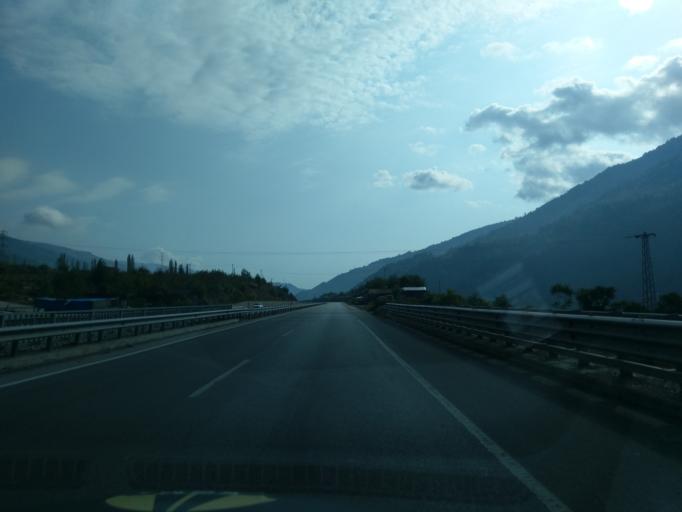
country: TR
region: Amasya
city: Akdag
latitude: 40.7466
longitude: 36.0333
